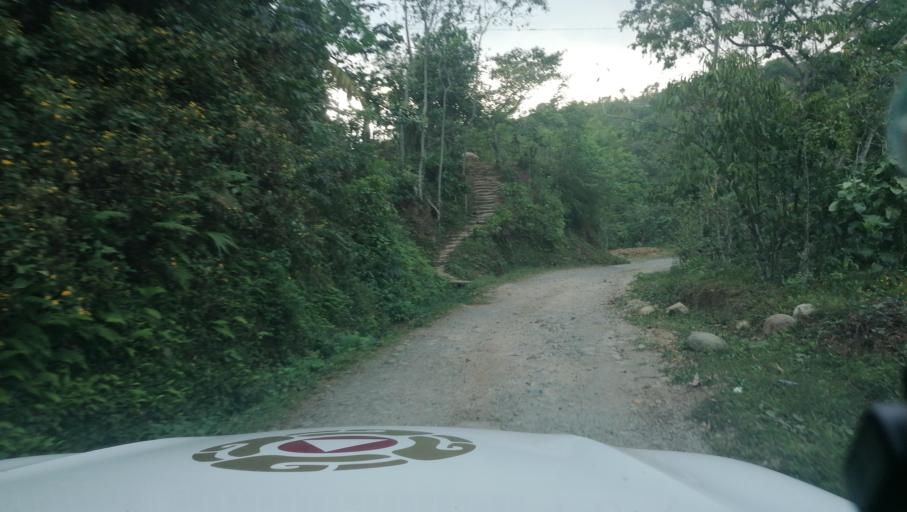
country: MX
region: Chiapas
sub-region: Cacahoatan
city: Benito Juarez
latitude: 15.1010
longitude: -92.2183
